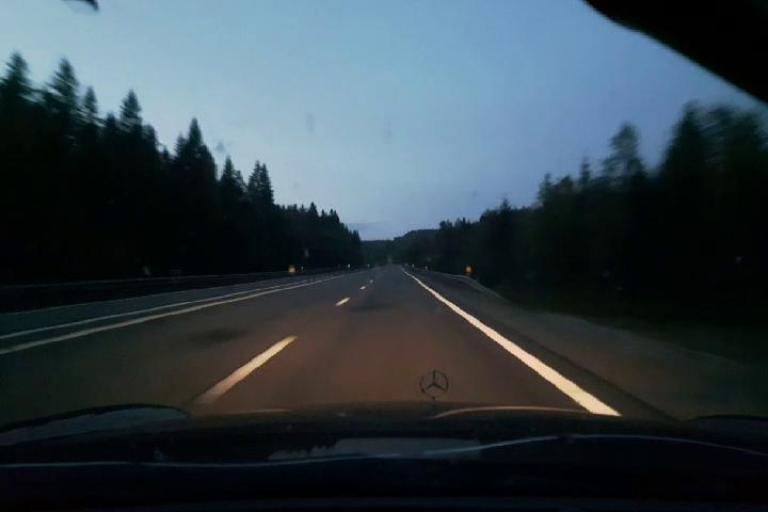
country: SE
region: Vaesternorrland
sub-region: Kramfors Kommun
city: Nordingra
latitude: 63.0774
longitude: 18.3639
